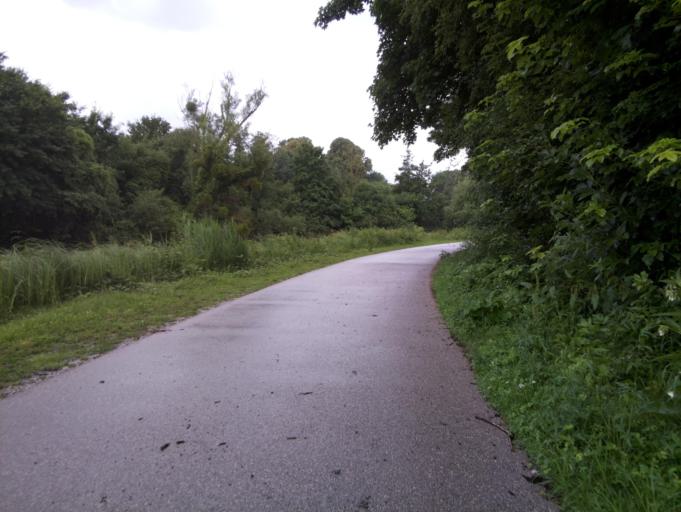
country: FR
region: Picardie
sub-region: Departement de la Somme
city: Ailly-sur-Somme
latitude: 49.9366
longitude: 2.1813
